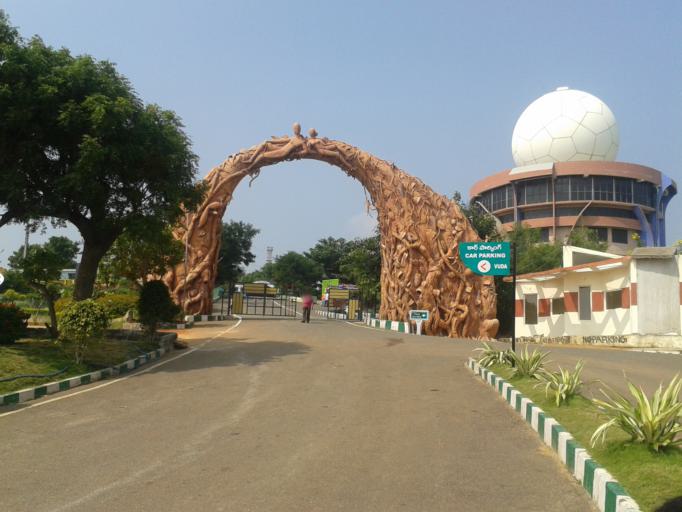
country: IN
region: Andhra Pradesh
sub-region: Vishakhapatnam
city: Yarada
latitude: 17.7476
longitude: 83.3461
